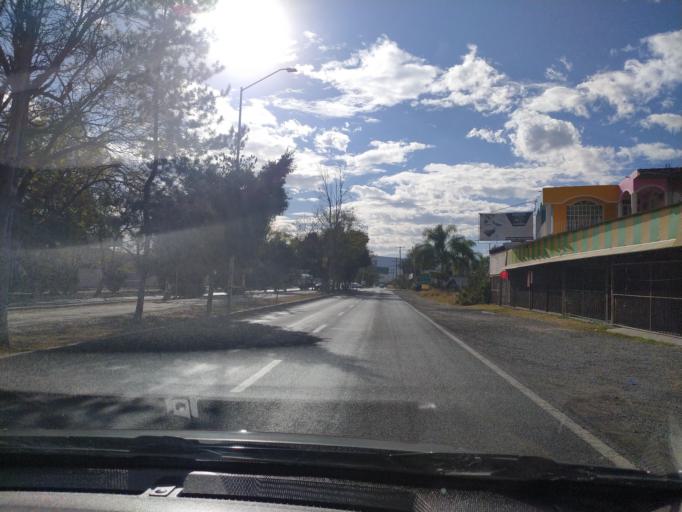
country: LA
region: Oudomxai
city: Muang La
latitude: 21.0325
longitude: 101.8375
